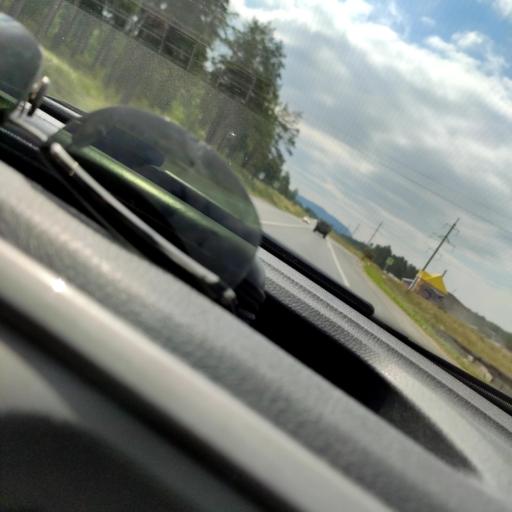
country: RU
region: Samara
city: Kurumoch
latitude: 53.4618
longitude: 50.0787
